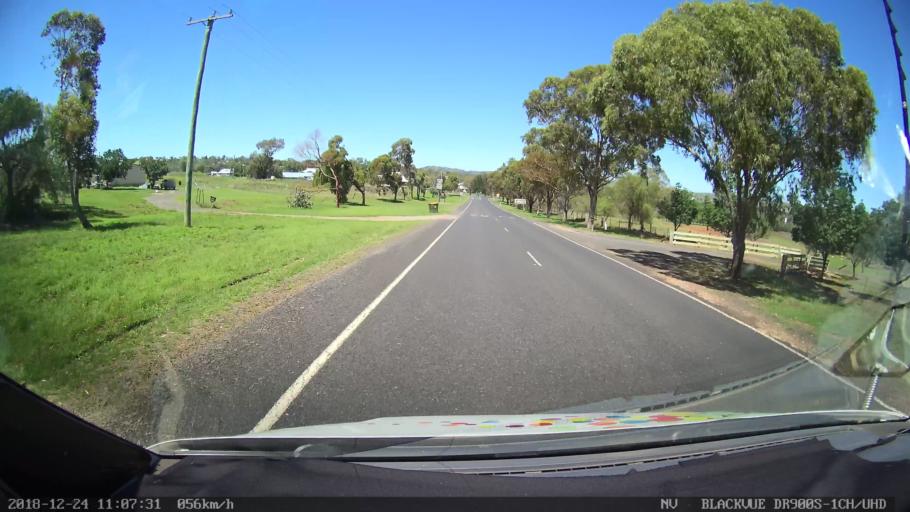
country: AU
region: New South Wales
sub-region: Upper Hunter Shire
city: Merriwa
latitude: -32.1336
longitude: 150.3593
